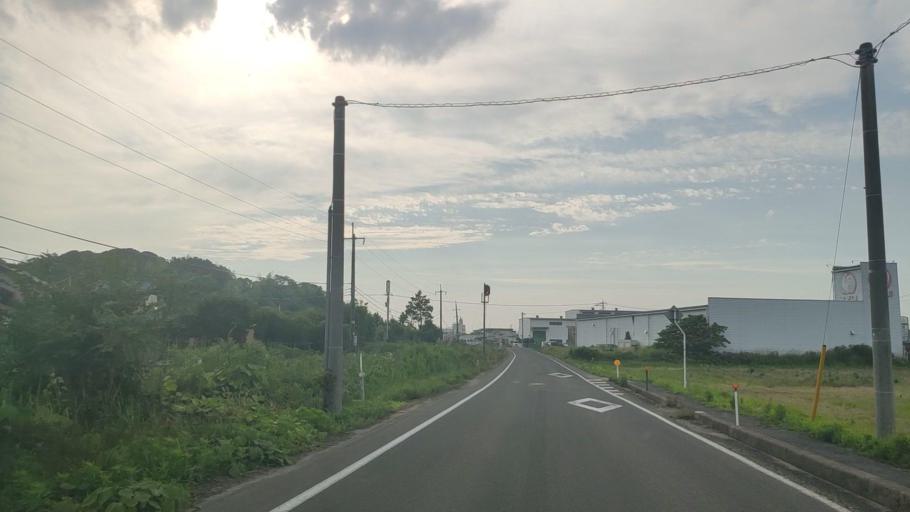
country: JP
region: Tottori
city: Kurayoshi
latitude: 35.4803
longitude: 133.8141
